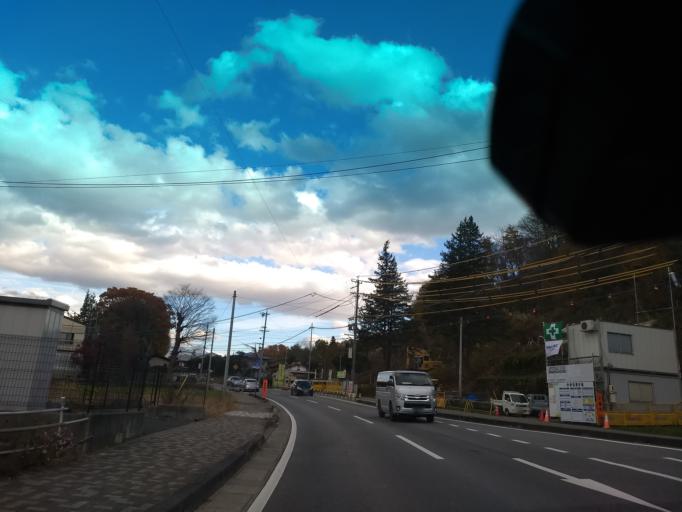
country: JP
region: Nagano
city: Chino
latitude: 35.9967
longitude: 138.1247
